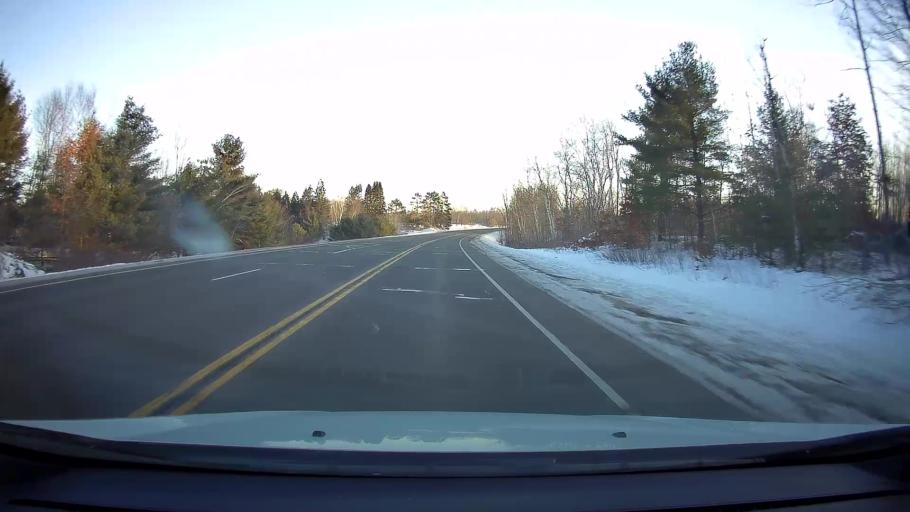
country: US
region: Wisconsin
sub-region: Barron County
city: Turtle Lake
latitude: 45.4605
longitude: -92.1000
